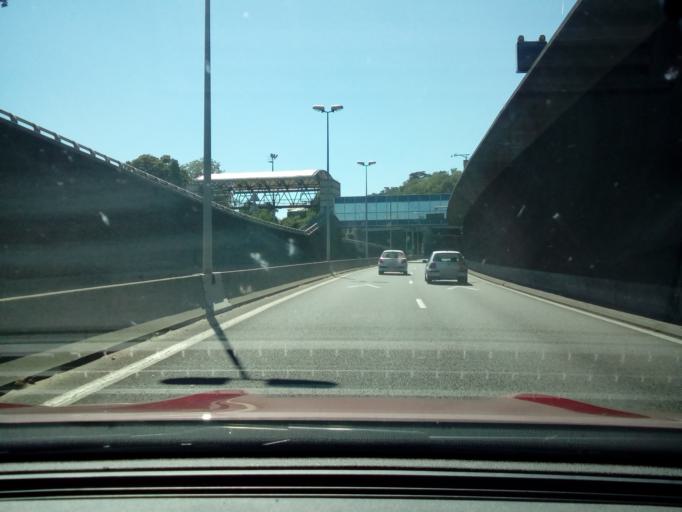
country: FR
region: Rhone-Alpes
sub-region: Departement du Rhone
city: Ecully
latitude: 45.7817
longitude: 4.7997
